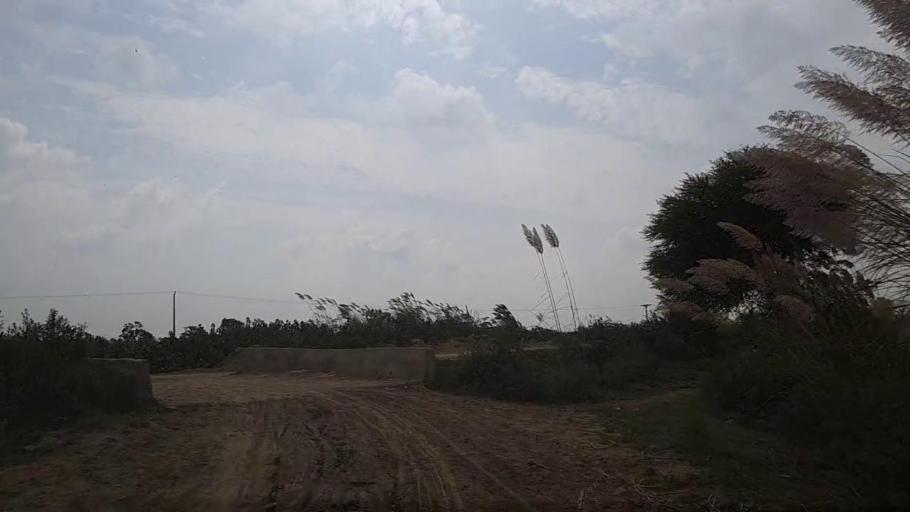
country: PK
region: Sindh
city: Mirpur Batoro
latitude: 24.6028
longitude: 68.1395
